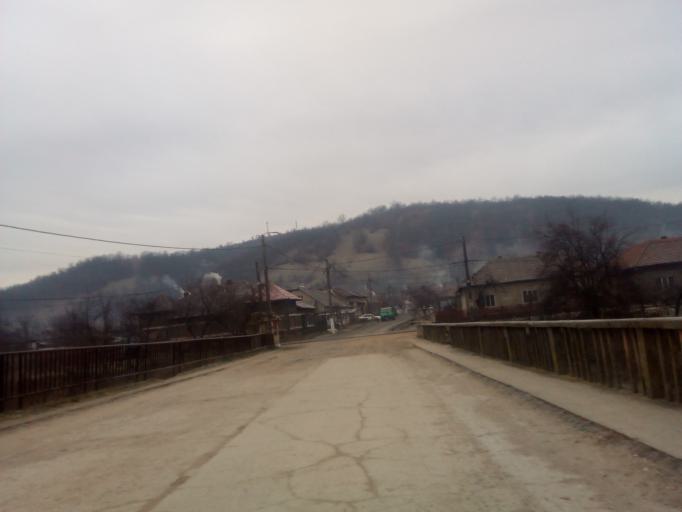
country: RO
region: Mehedinti
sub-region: Comuna Eselnita
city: Eselnita
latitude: 44.6952
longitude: 22.3669
